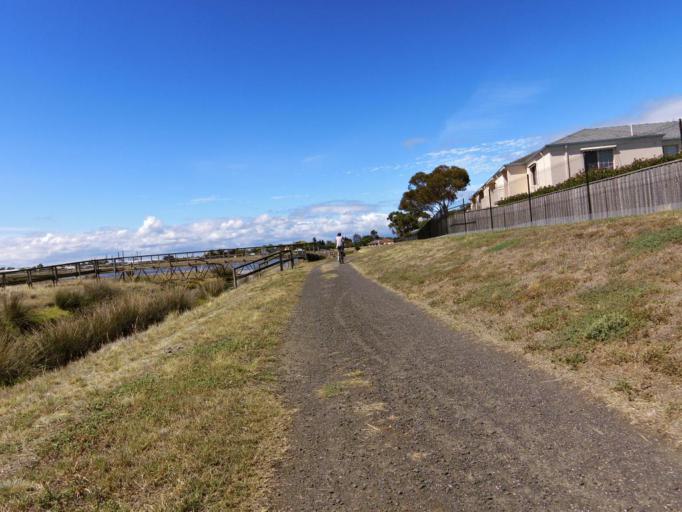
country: AU
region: Victoria
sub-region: Hobsons Bay
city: Altona Meadows
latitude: -37.8711
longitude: 144.8030
